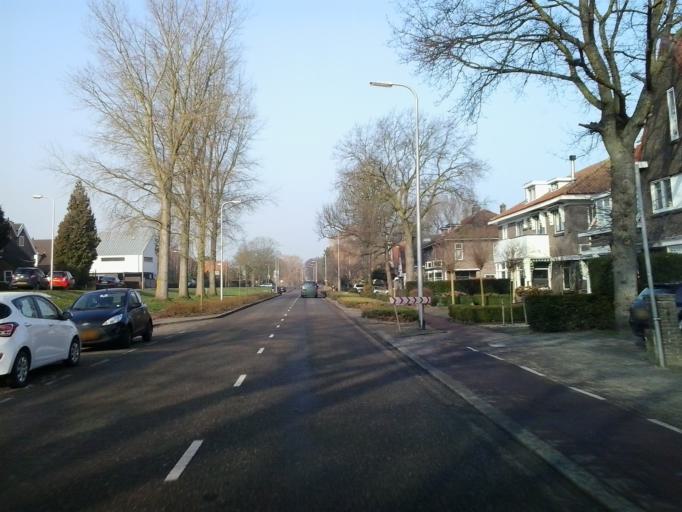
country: NL
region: South Holland
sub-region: Gemeente Ridderkerk
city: Ridderkerk
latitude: 51.8556
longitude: 4.5830
